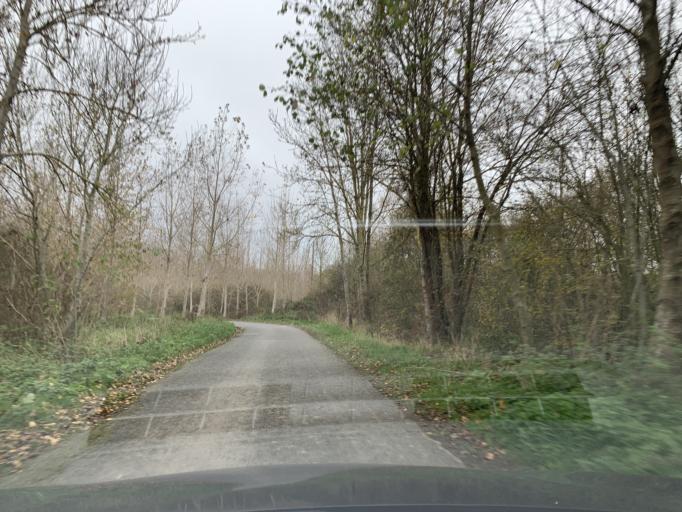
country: FR
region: Nord-Pas-de-Calais
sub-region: Departement du Pas-de-Calais
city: Ecourt-Saint-Quentin
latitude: 50.2512
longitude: 3.0977
